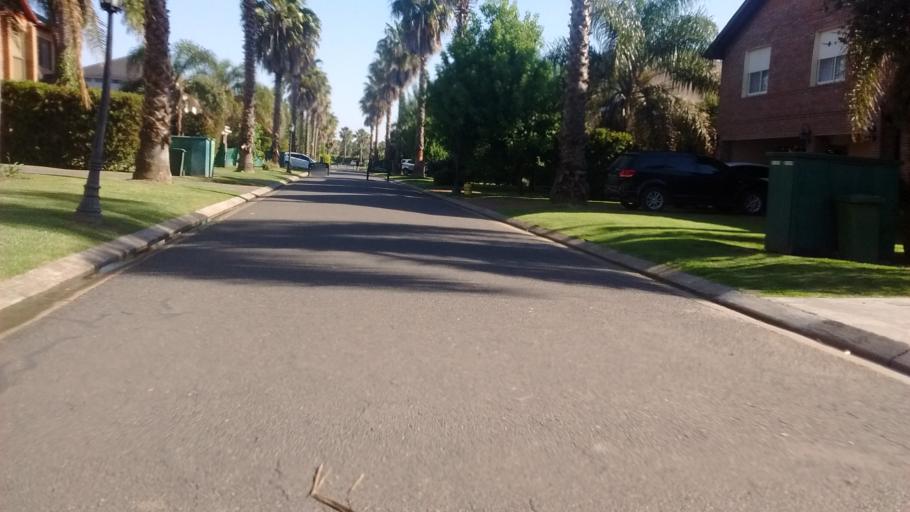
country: AR
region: Santa Fe
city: Funes
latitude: -32.9243
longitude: -60.8213
